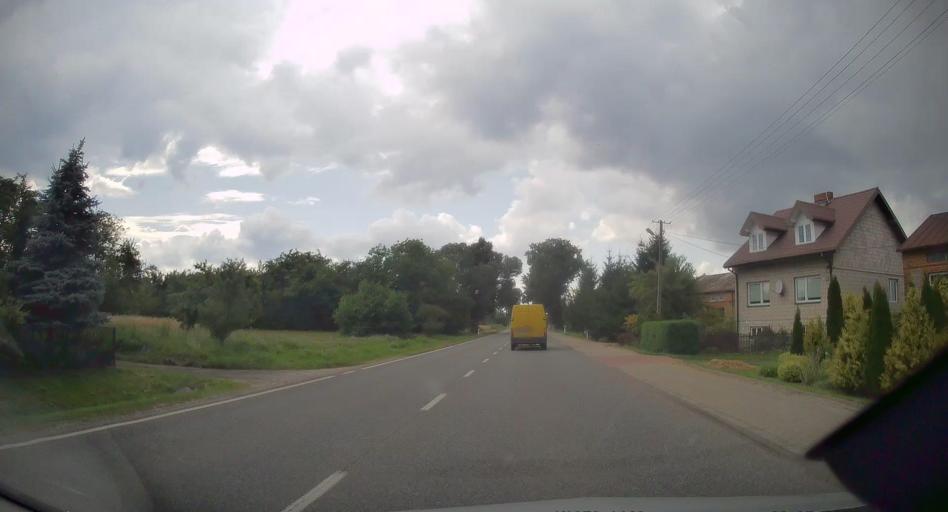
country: PL
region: Lodz Voivodeship
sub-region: Powiat skierniewicki
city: Gluchow
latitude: 51.7747
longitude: 20.1279
